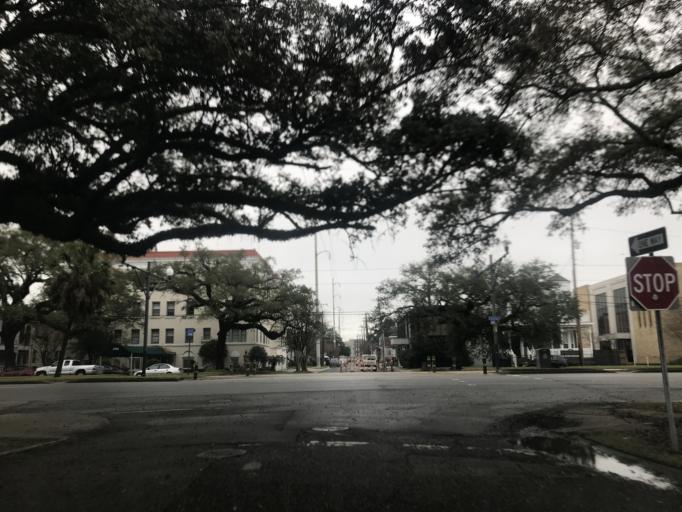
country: US
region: Louisiana
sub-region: Orleans Parish
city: New Orleans
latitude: 29.9717
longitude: -90.0970
